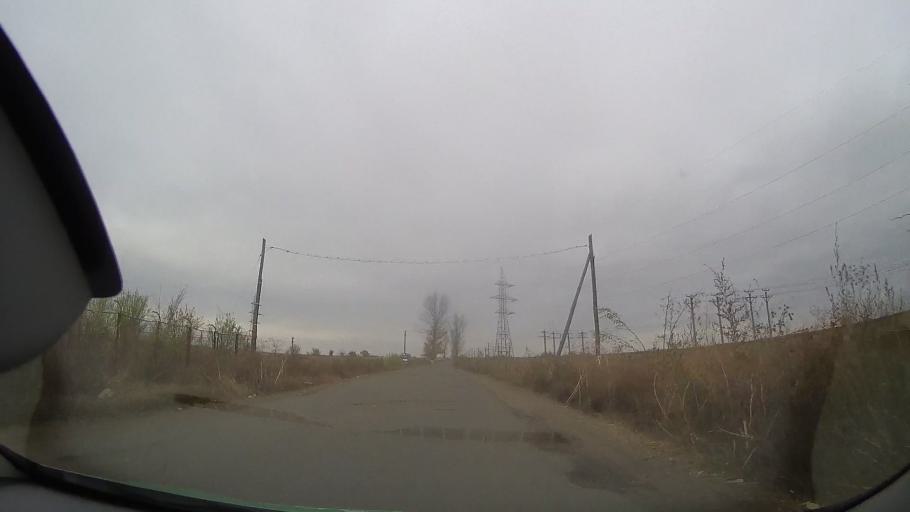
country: RO
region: Braila
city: Dudesti
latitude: 44.8971
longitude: 27.4331
